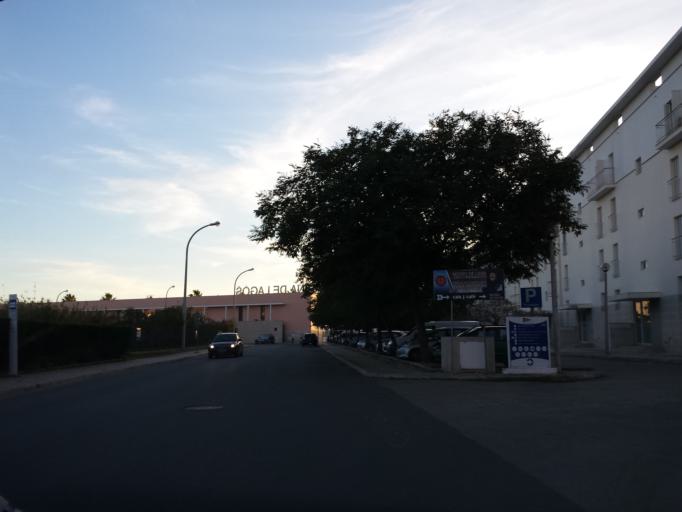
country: PT
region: Faro
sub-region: Lagos
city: Lagos
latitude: 37.1106
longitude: -8.6728
